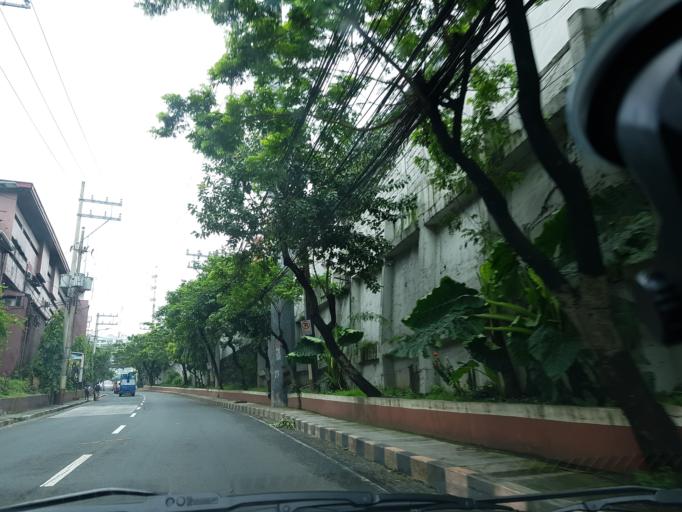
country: PH
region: Metro Manila
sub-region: Pasig
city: Pasig City
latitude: 14.5718
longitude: 121.0681
